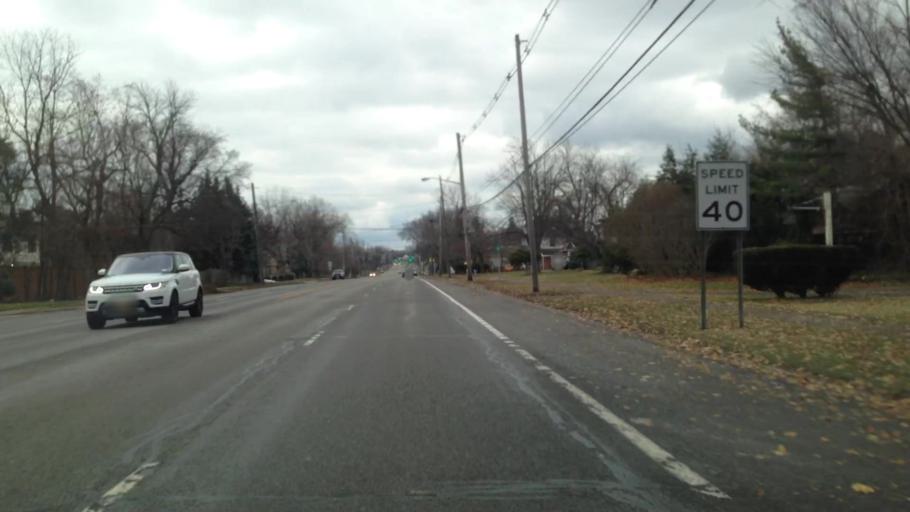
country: US
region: New York
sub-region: Erie County
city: Eggertsville
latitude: 42.9642
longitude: -78.7963
